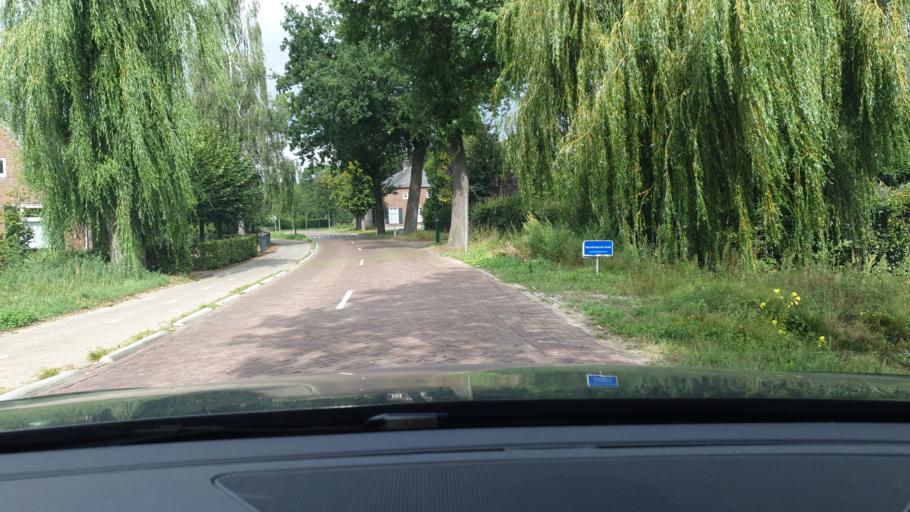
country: NL
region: North Brabant
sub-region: Gemeente Son en Breugel
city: Breugel
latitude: 51.4994
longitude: 5.5130
